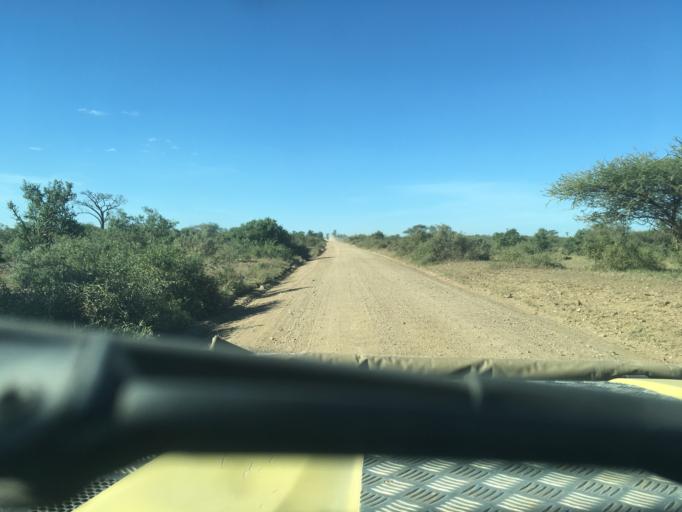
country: TZ
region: Mara
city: Mugumu
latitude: -2.3912
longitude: 34.8151
